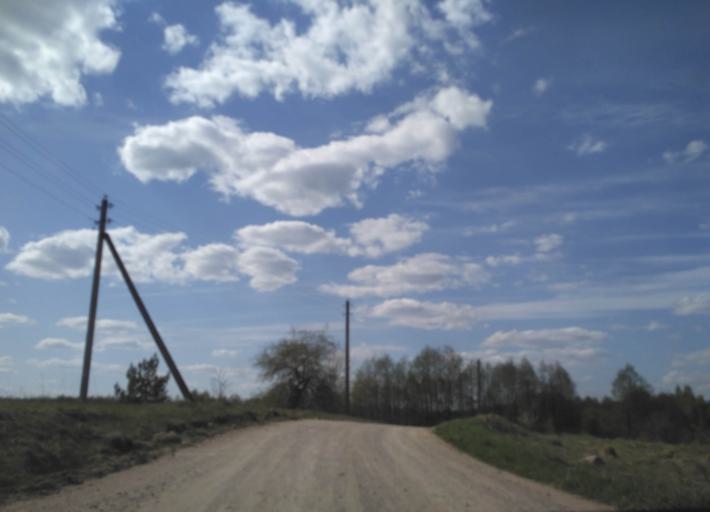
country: BY
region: Minsk
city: Narach
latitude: 54.9898
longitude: 26.5928
